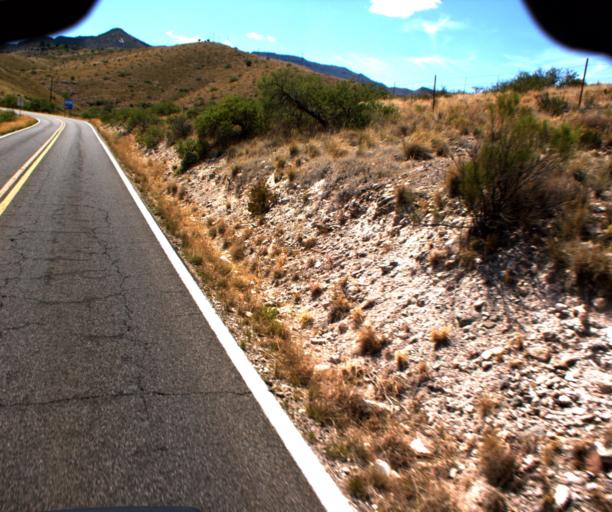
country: US
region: Arizona
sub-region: Yavapai County
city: Clarkdale
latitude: 34.7583
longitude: -112.0863
